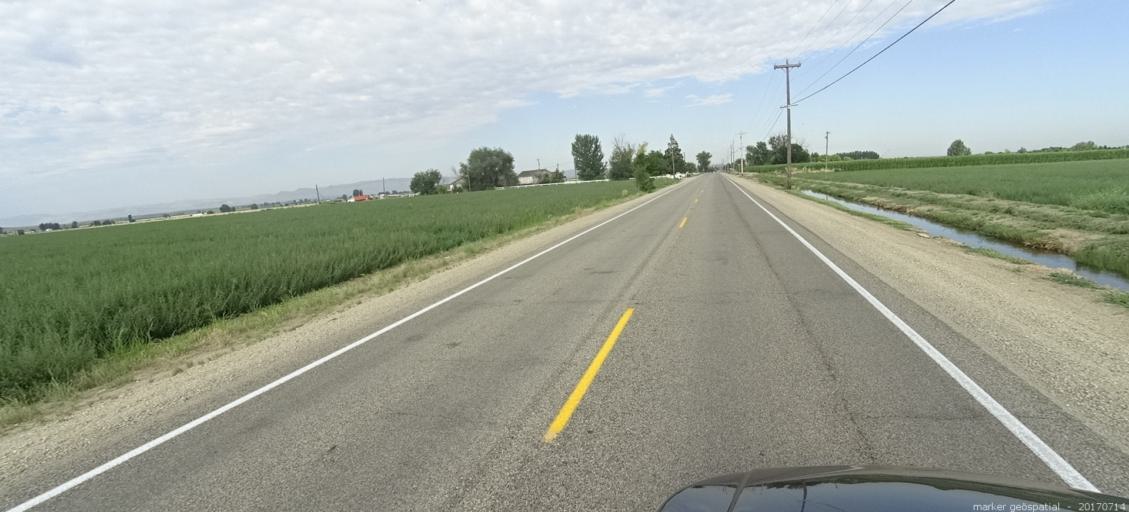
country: US
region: Idaho
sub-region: Ada County
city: Kuna
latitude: 43.4883
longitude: -116.4615
